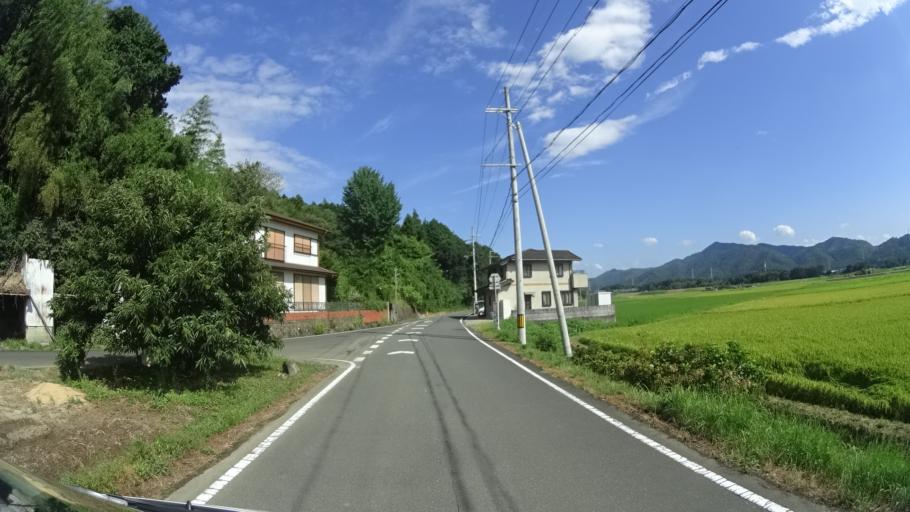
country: JP
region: Kyoto
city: Ayabe
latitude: 35.3171
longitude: 135.1875
